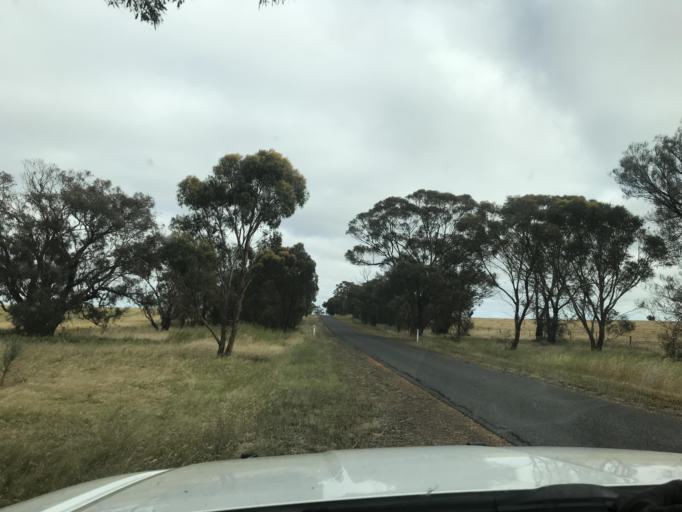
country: AU
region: South Australia
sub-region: Tatiara
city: Bordertown
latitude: -36.3440
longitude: 141.0908
